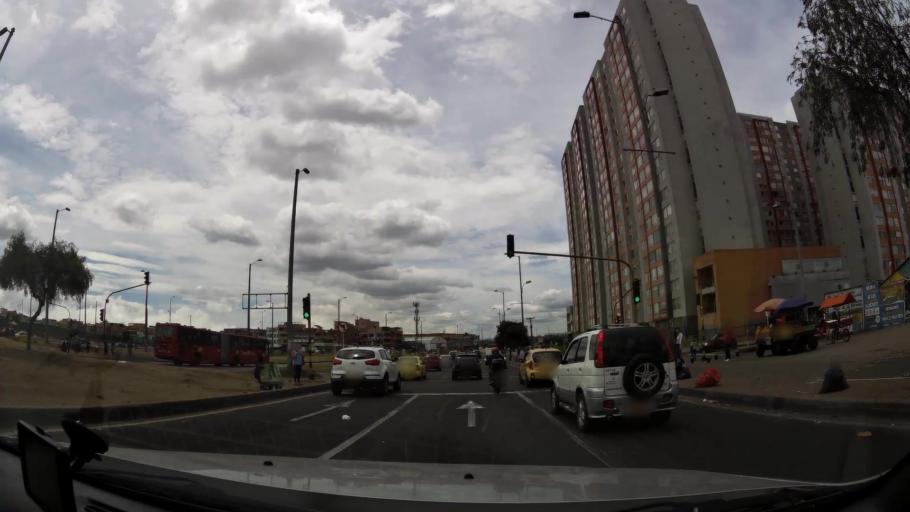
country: CO
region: Bogota D.C.
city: Bogota
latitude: 4.6358
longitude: -74.1531
